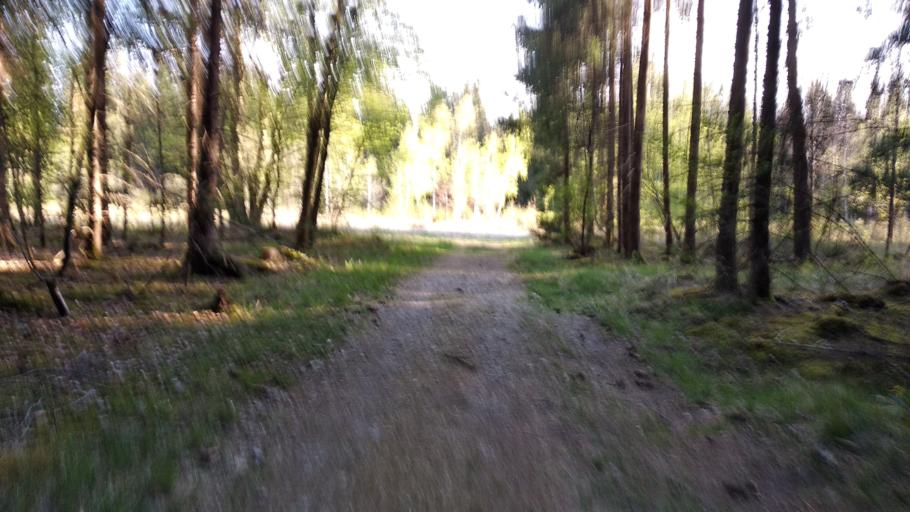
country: DE
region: Bavaria
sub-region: Upper Bavaria
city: Grasbrunn
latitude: 48.0980
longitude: 11.7459
